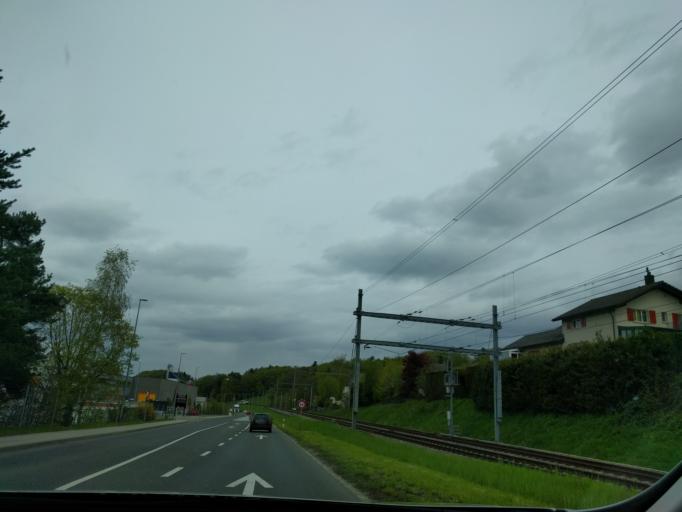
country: CH
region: Fribourg
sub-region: Sense District
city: Dudingen
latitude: 46.8546
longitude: 7.1954
